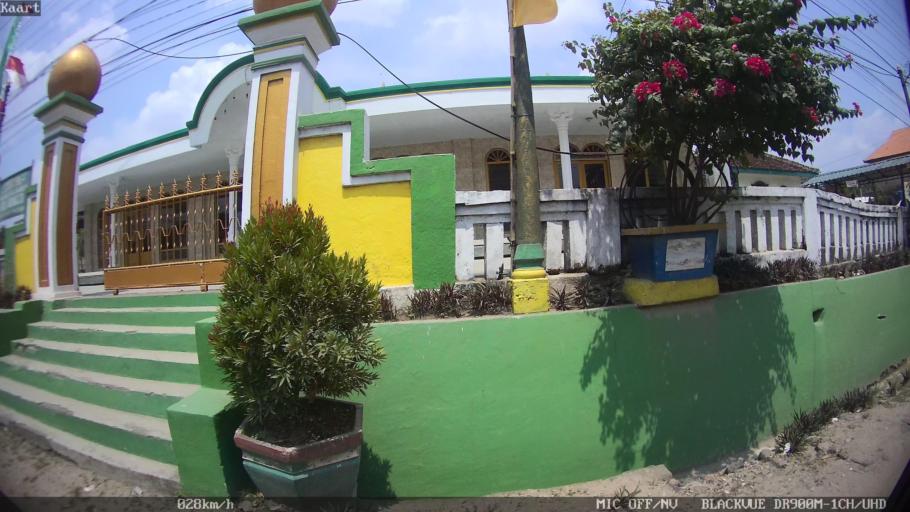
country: ID
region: Lampung
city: Pringsewu
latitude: -5.3486
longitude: 104.9757
